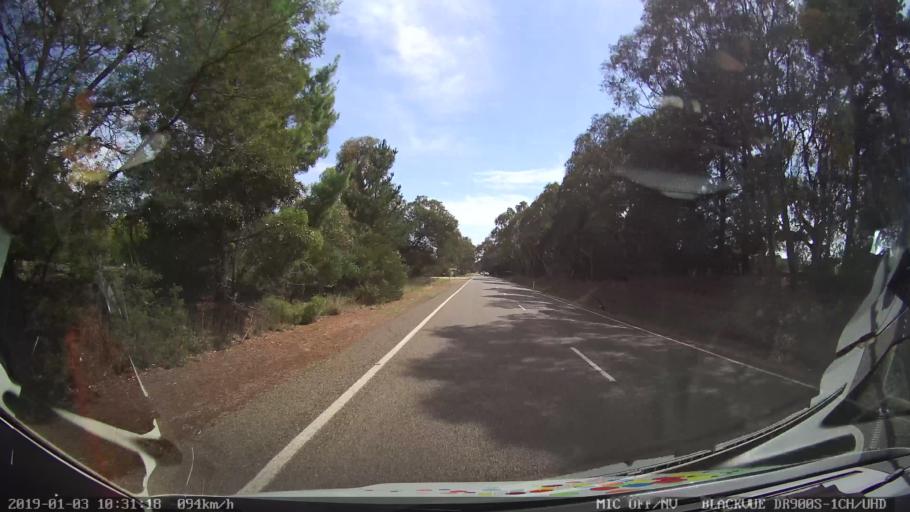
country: AU
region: New South Wales
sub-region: Young
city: Young
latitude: -34.3518
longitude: 148.2759
